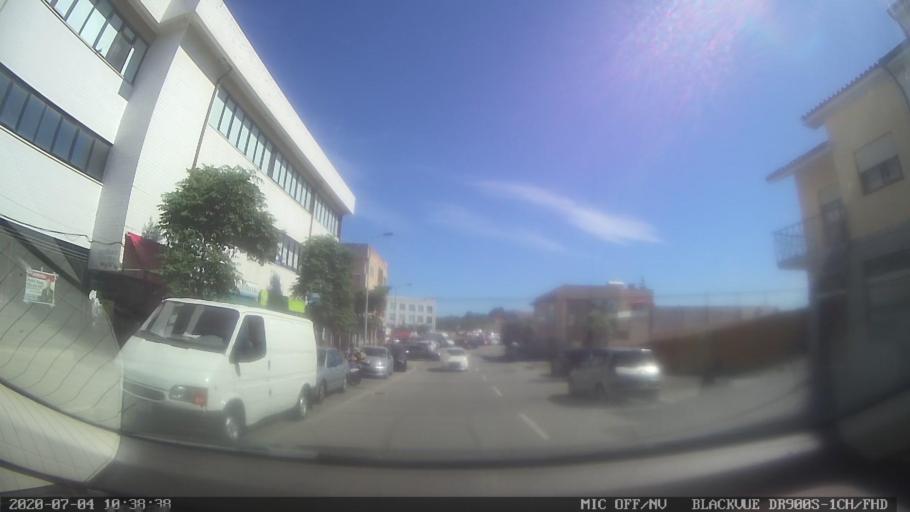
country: PT
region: Porto
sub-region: Matosinhos
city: Lavra
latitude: 41.2592
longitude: -8.7175
